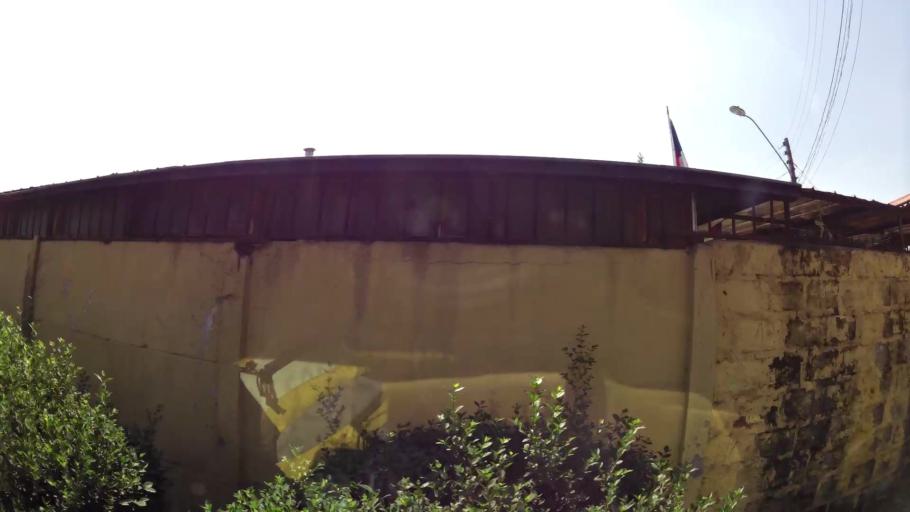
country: CL
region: Santiago Metropolitan
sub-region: Provincia de Santiago
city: La Pintana
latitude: -33.5527
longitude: -70.6007
